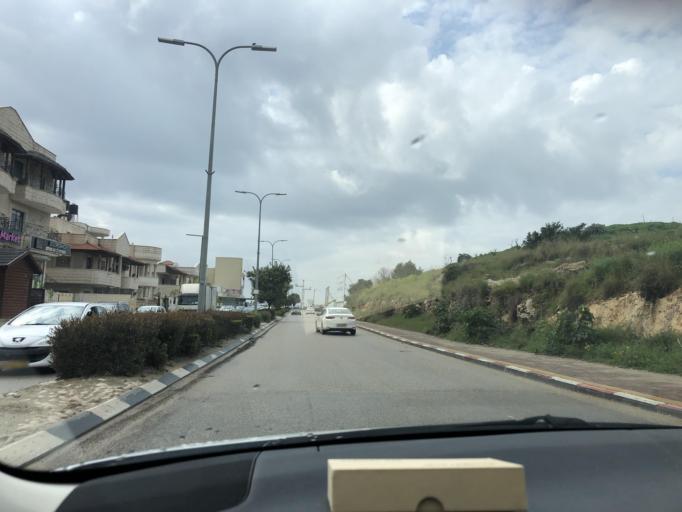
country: IL
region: Central District
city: Kafr Qasim
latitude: 32.1116
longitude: 34.9663
